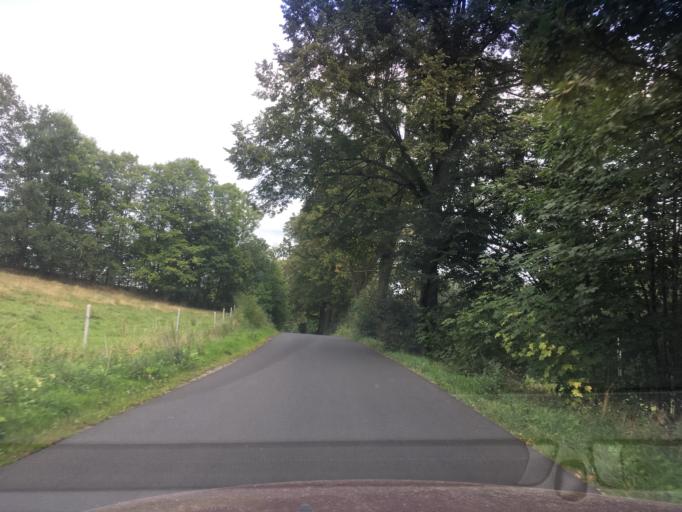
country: PL
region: Lower Silesian Voivodeship
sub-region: Powiat jeleniogorski
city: Stara Kamienica
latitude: 50.8968
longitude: 15.5658
